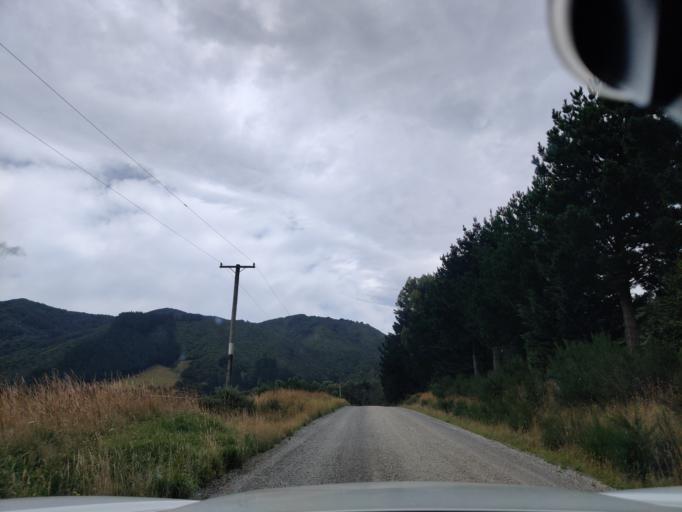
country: NZ
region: Wellington
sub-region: Masterton District
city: Masterton
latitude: -41.0373
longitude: 175.4013
